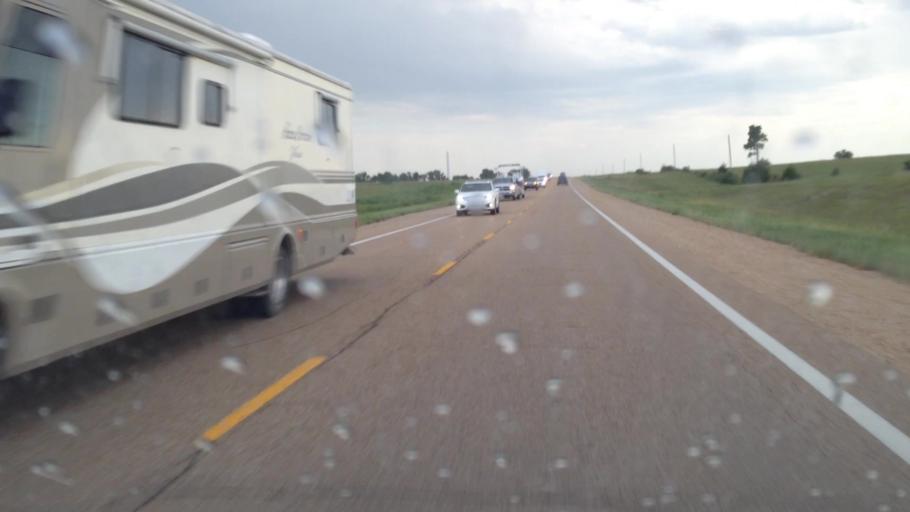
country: US
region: Kansas
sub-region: Coffey County
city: Burlington
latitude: 38.1481
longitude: -95.7392
